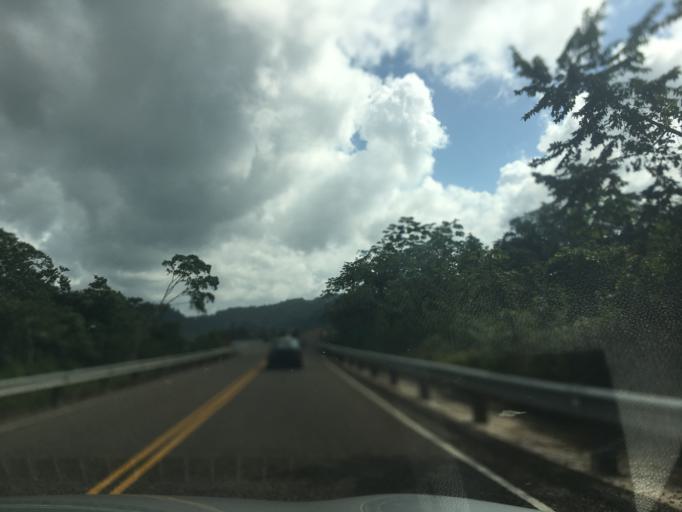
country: BZ
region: Cayo
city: Belmopan
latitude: 17.1494
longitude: -88.7106
